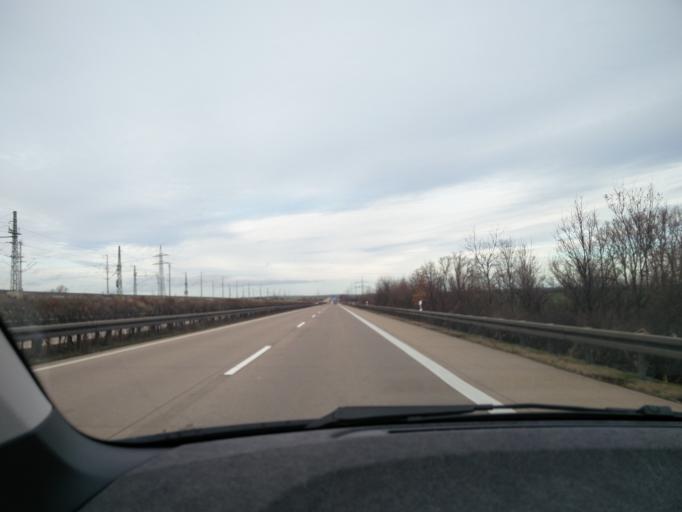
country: DE
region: Thuringia
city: Ichtershausen
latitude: 50.8726
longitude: 10.9930
